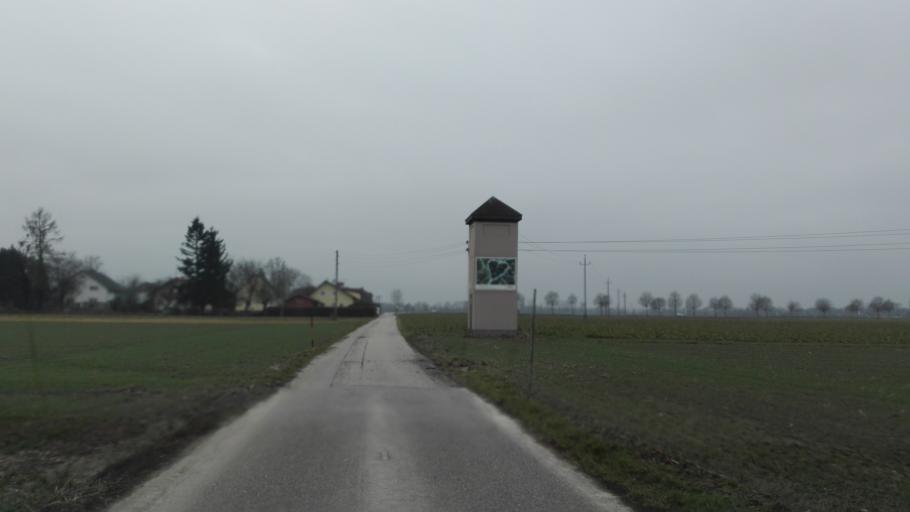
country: AT
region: Upper Austria
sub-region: Politischer Bezirk Linz-Land
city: Horsching
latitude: 48.2308
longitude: 14.1520
